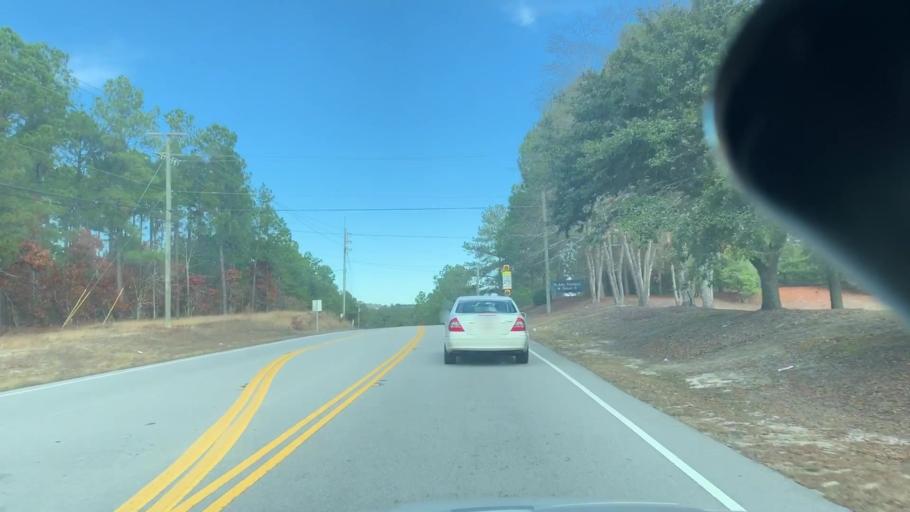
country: US
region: South Carolina
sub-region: Richland County
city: Woodfield
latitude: 34.0885
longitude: -80.8912
